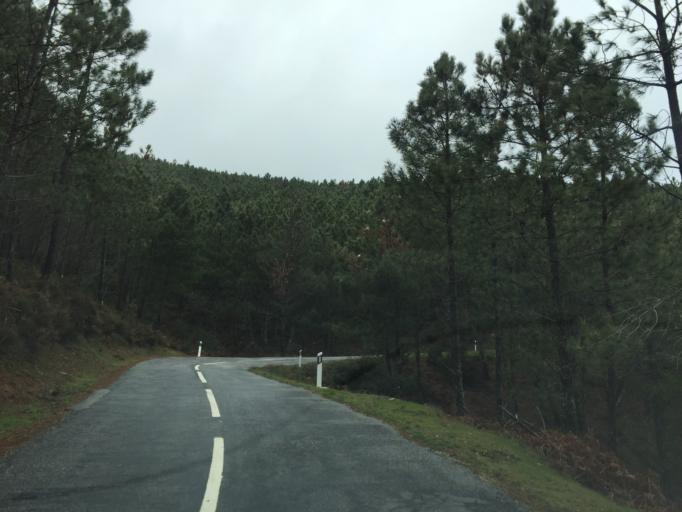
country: PT
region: Guarda
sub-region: Seia
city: Seia
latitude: 40.3366
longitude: -7.7162
